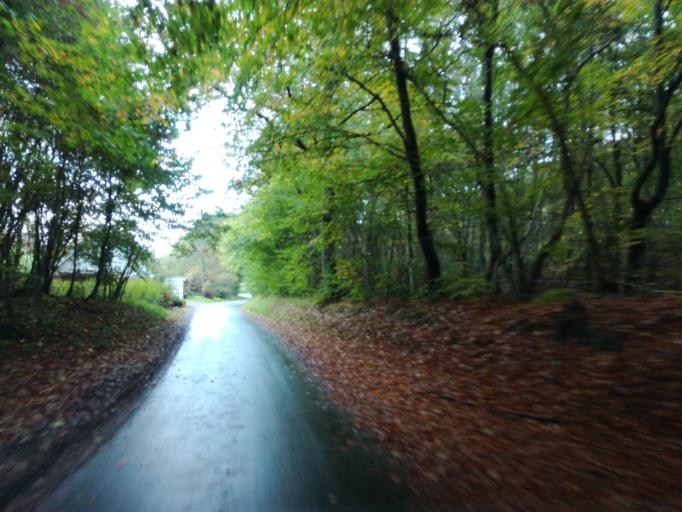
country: DK
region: South Denmark
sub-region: Vejle Kommune
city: Borkop
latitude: 55.6336
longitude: 9.6577
